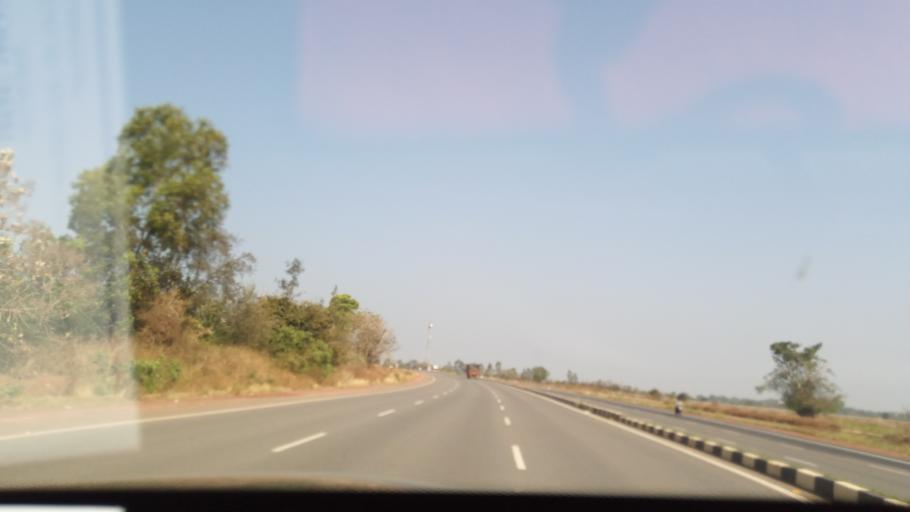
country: IN
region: Karnataka
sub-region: Haveri
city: Shiggaon
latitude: 15.0533
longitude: 75.1681
